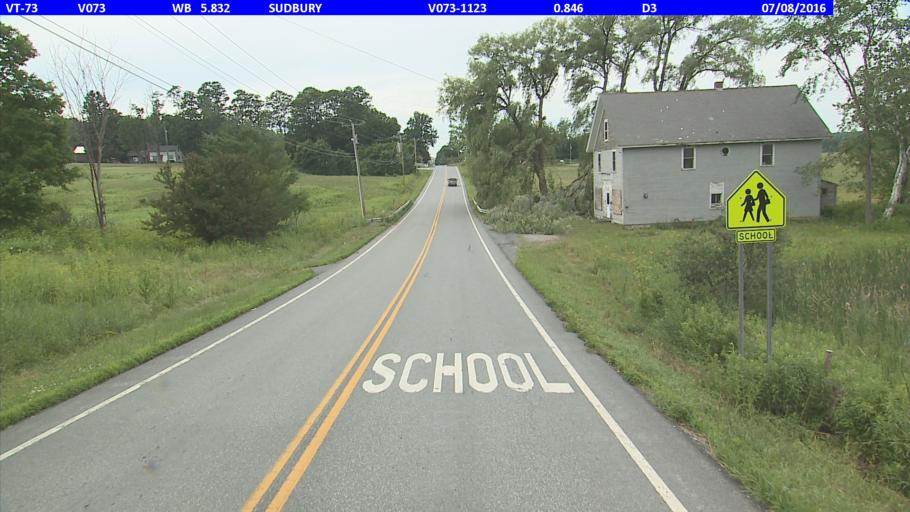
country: US
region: Vermont
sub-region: Rutland County
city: Brandon
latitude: 43.8228
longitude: -73.1839
